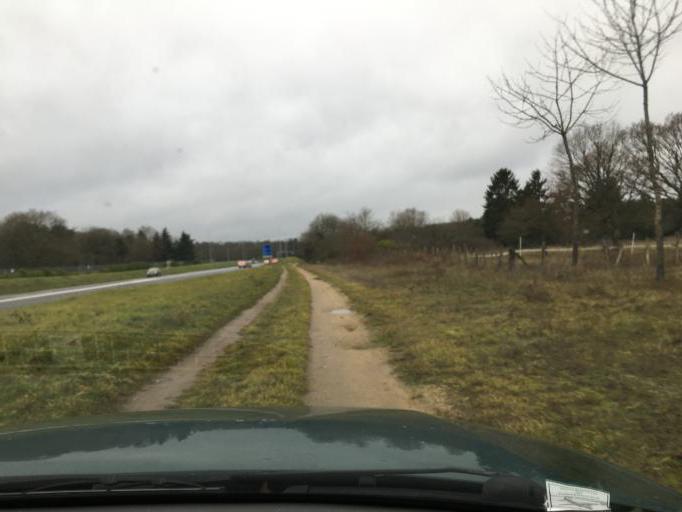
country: FR
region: Centre
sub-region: Departement du Loiret
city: Olivet
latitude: 47.8412
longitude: 1.8822
